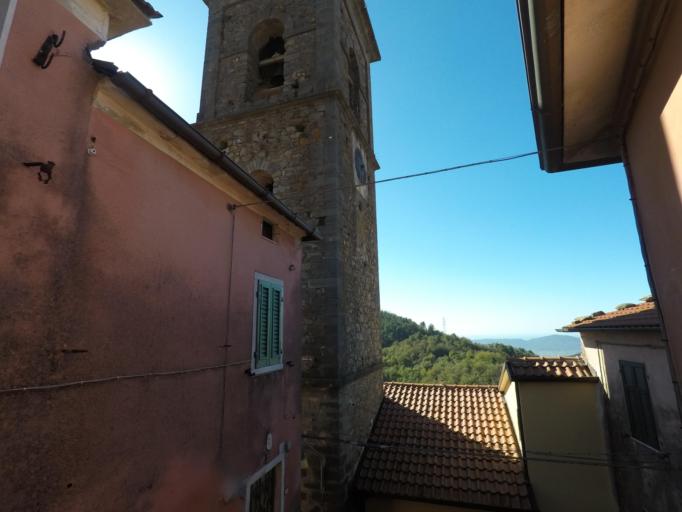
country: IT
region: Liguria
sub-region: Provincia di La Spezia
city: Casano-Dogana-Isola
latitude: 44.1110
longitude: 10.0754
